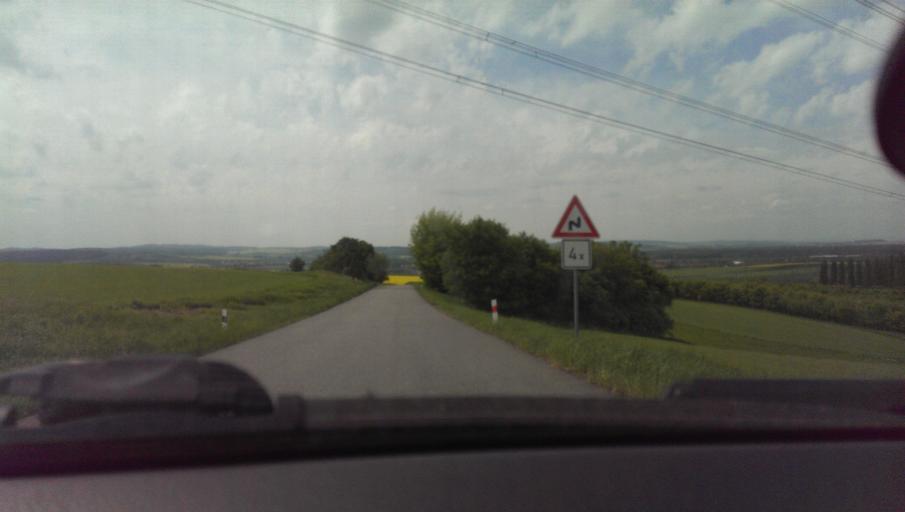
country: CZ
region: Zlin
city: Tlumacov
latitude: 49.2557
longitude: 17.5314
